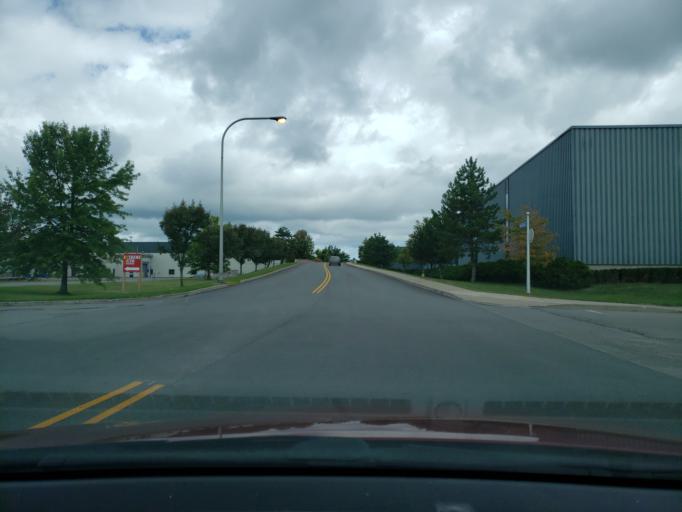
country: US
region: New York
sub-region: Monroe County
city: North Gates
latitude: 43.1507
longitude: -77.7407
